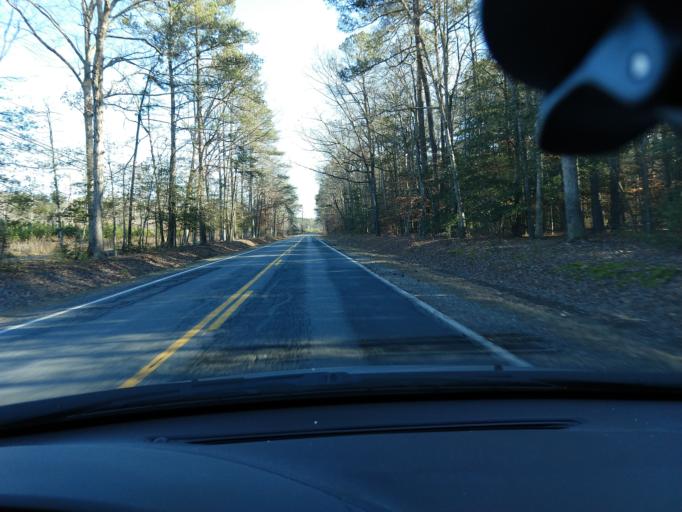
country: US
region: Virginia
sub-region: Charles City County
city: Charles City
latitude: 37.3238
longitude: -76.9786
